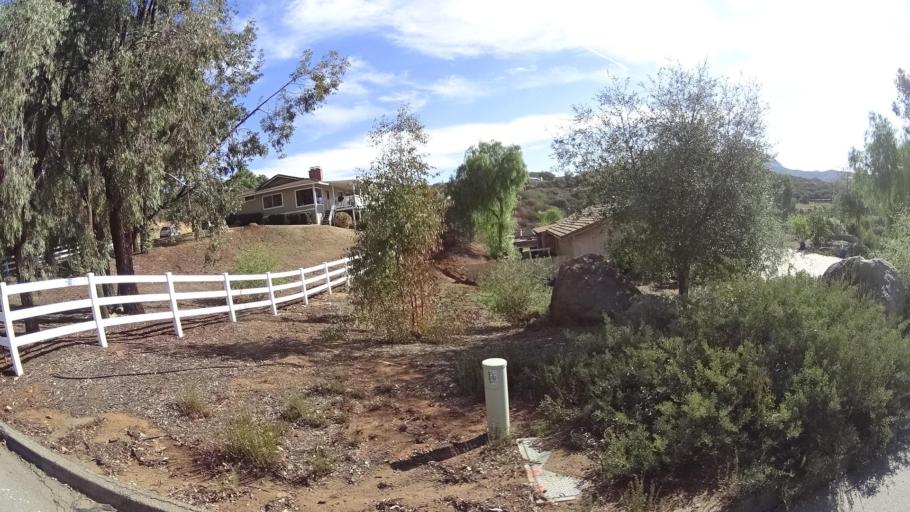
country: US
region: California
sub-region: San Diego County
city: Alpine
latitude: 32.8217
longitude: -116.7422
